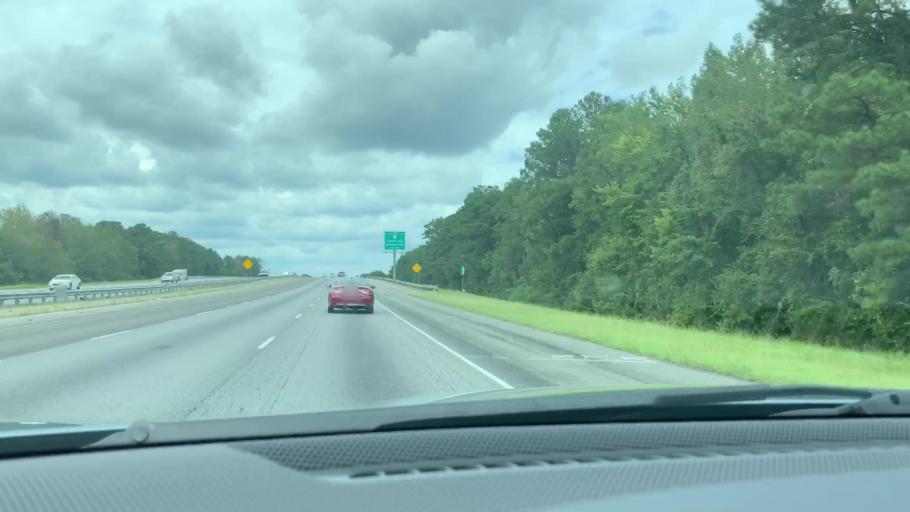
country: US
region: Georgia
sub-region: Bryan County
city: Richmond Hill
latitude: 31.9078
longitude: -81.3347
